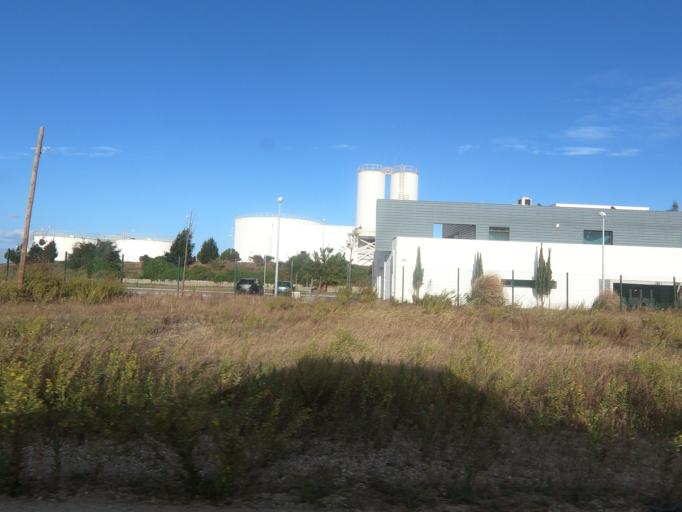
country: PT
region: Setubal
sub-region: Barreiro
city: Barreiro
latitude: 38.6747
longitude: -9.0463
